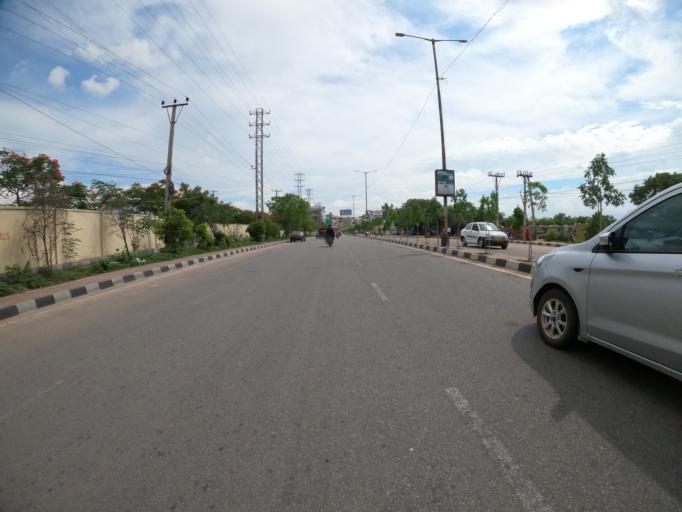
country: IN
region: Telangana
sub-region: Hyderabad
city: Hyderabad
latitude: 17.3675
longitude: 78.3998
